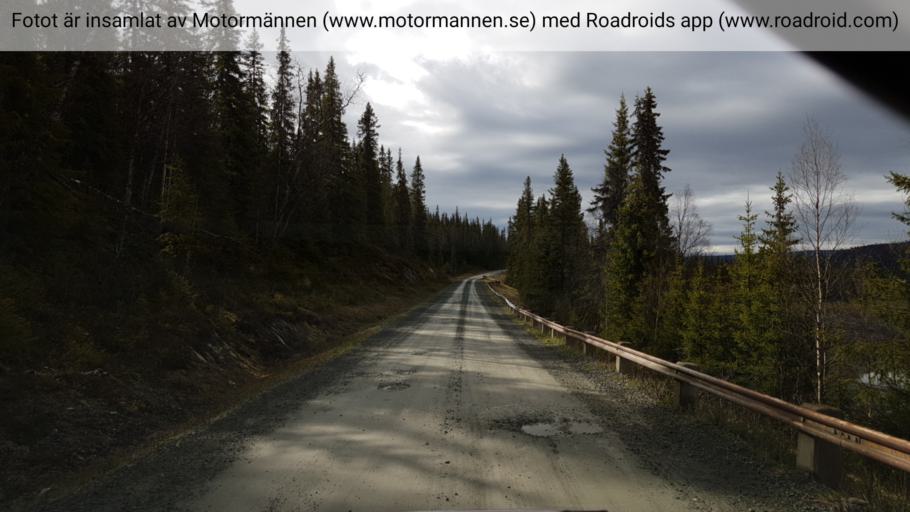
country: SE
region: Vaesterbotten
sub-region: Vilhelmina Kommun
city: Sjoberg
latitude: 65.5330
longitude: 15.4348
